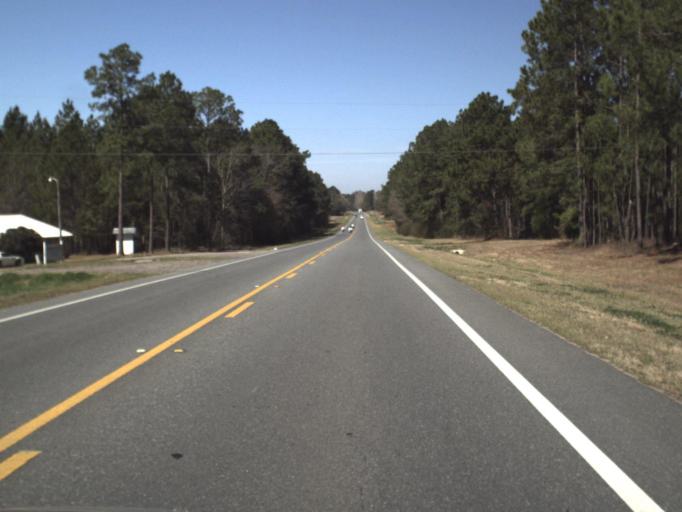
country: US
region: Florida
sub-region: Jackson County
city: Marianna
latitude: 30.7250
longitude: -85.0827
